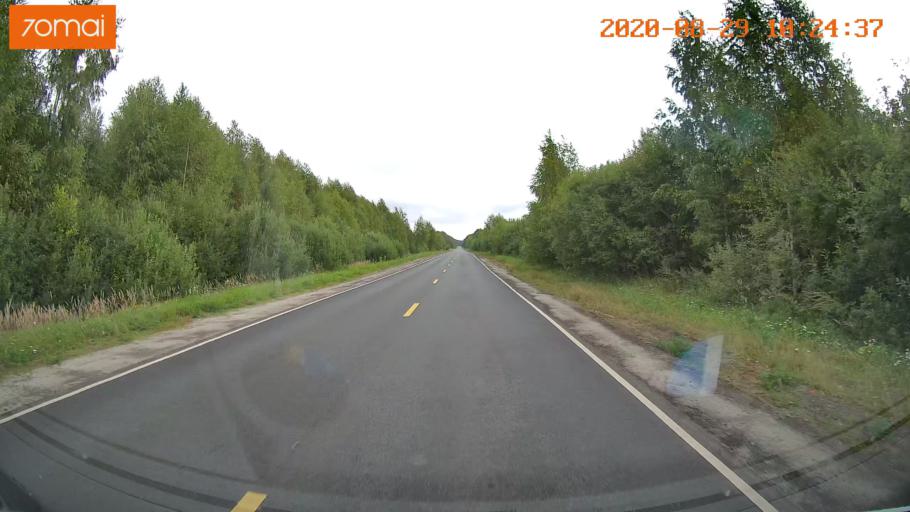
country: RU
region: Ivanovo
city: Yur'yevets
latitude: 57.3207
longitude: 43.0018
